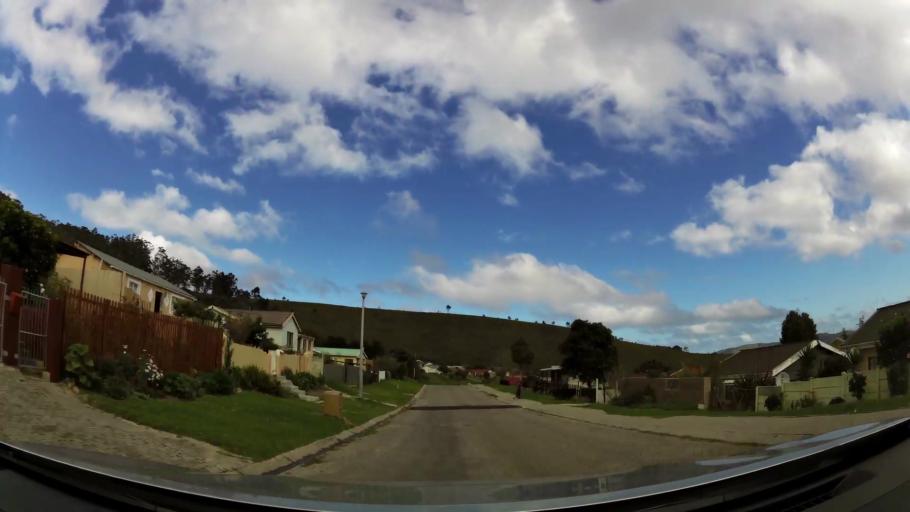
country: ZA
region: Western Cape
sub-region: Eden District Municipality
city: Knysna
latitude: -34.0524
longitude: 23.1056
